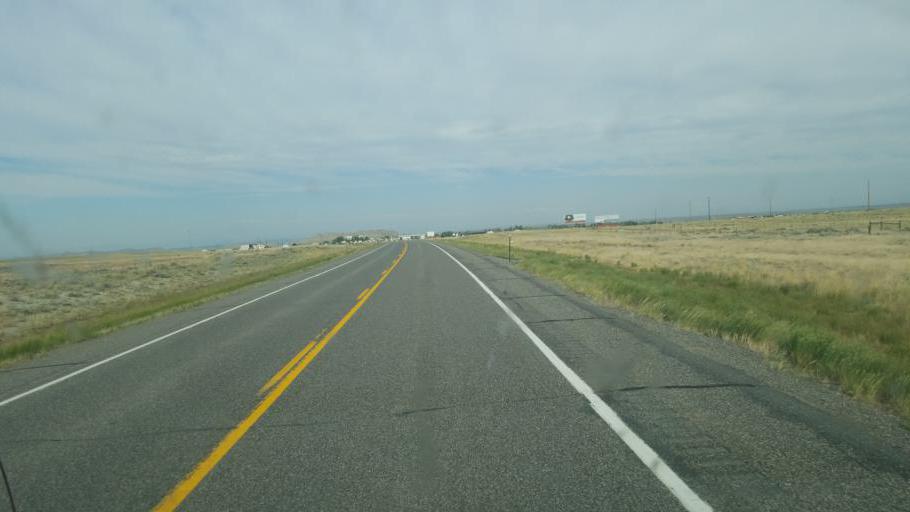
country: US
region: Wyoming
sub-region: Fremont County
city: Riverton
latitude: 43.2369
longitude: -108.0878
